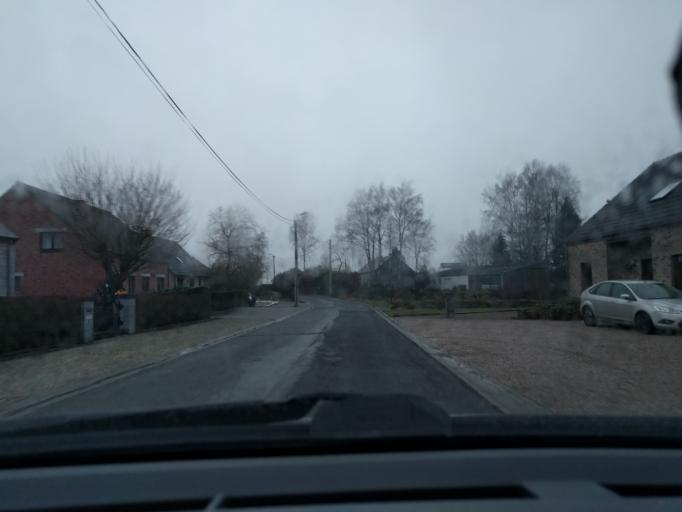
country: BE
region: Wallonia
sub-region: Province de Namur
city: Couvin
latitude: 50.0468
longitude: 4.5078
